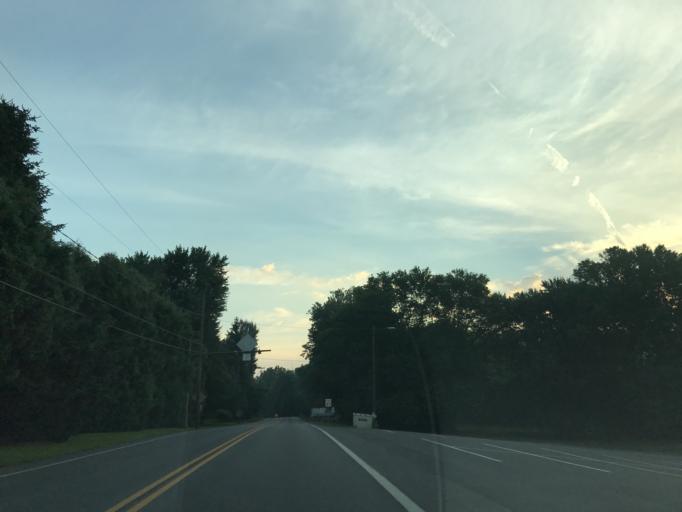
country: US
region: Pennsylvania
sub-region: Lancaster County
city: Lancaster
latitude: 40.0056
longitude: -76.3047
